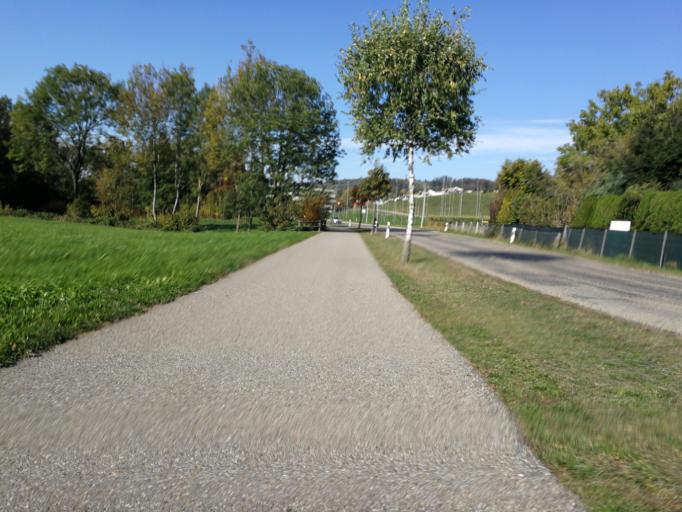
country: CH
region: Zurich
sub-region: Bezirk Hinwil
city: Hinwil
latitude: 47.2943
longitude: 8.8518
